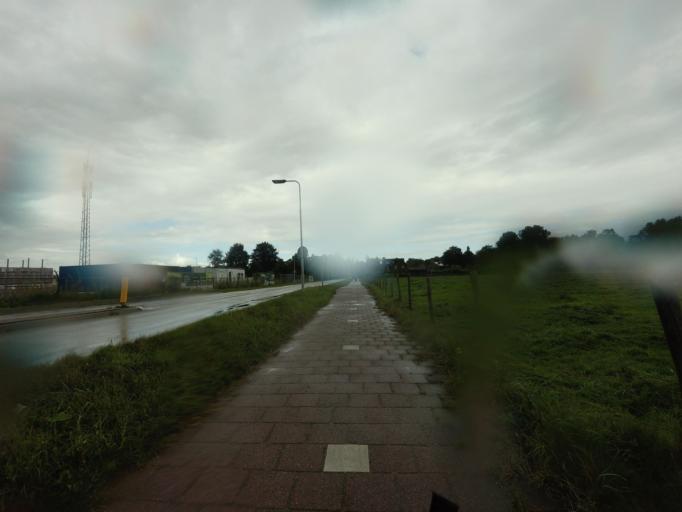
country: NL
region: North Holland
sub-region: Gemeente Wijdemeren
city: Nieuw-Loosdrecht
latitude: 52.1688
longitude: 5.1715
